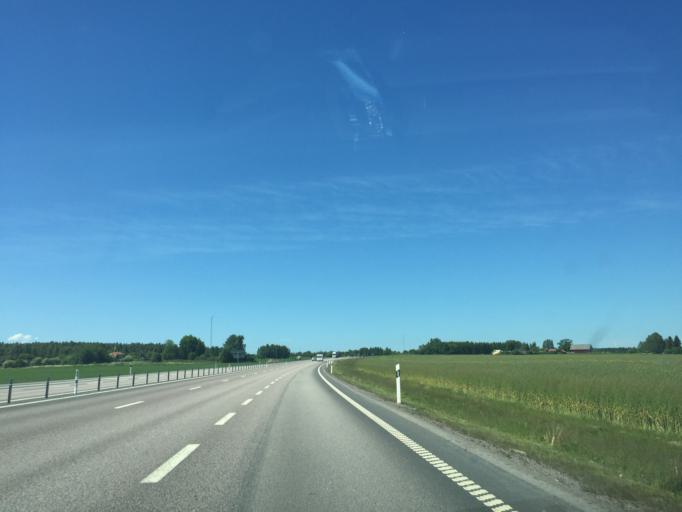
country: SE
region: OEstergoetland
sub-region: Motala Kommun
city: Stenstorp
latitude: 58.4045
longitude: 15.0882
